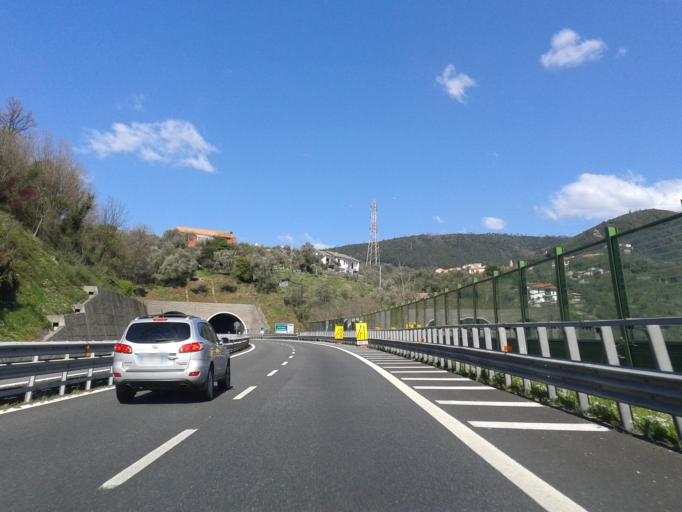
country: IT
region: Liguria
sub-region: Provincia di Genova
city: Sestri Levante
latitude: 44.2785
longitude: 9.4167
